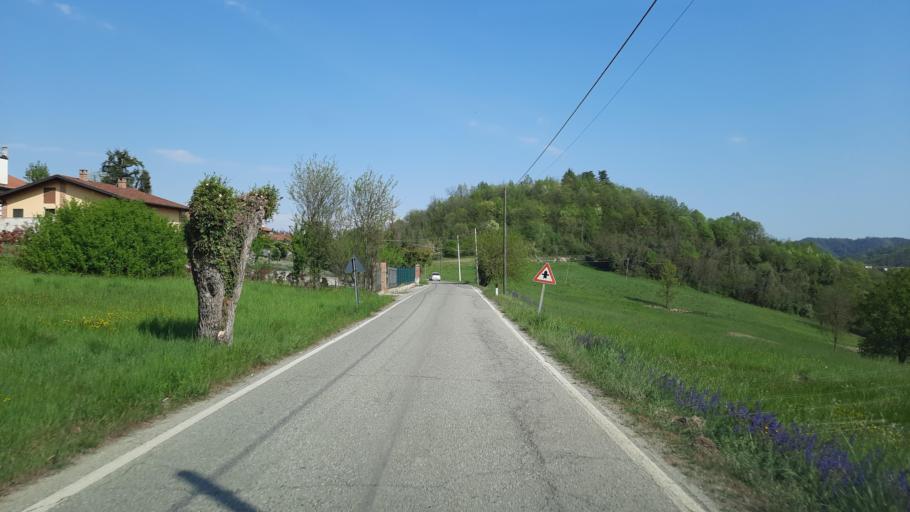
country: IT
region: Piedmont
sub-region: Provincia di Torino
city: Valentino
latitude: 45.1631
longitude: 8.1018
